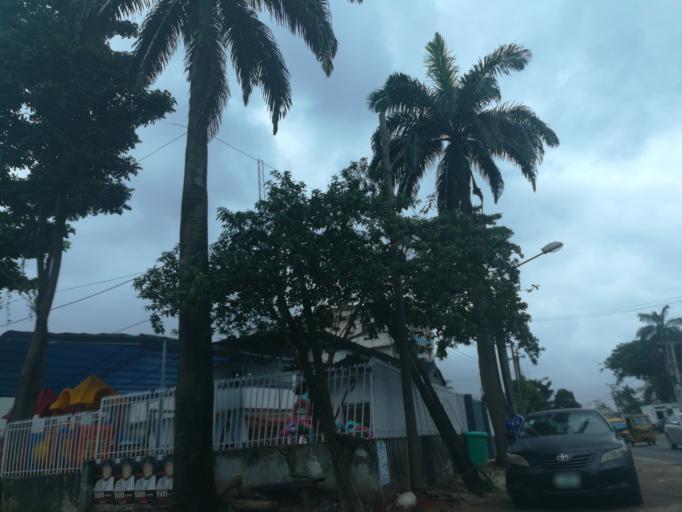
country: NG
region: Lagos
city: Agege
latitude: 6.6202
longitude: 3.3449
